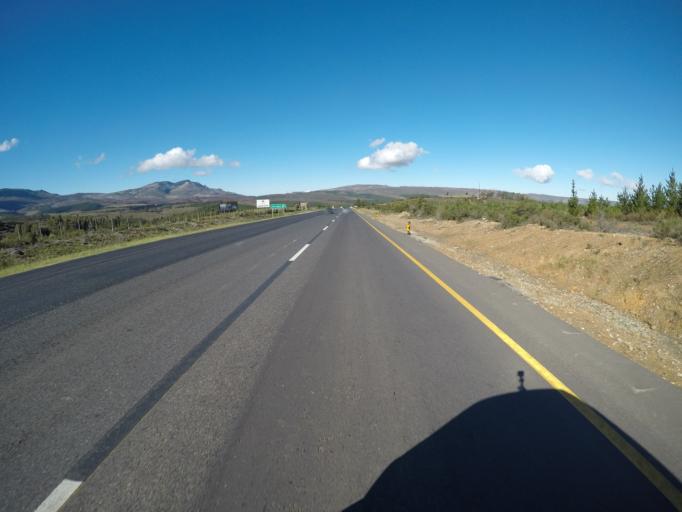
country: ZA
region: Western Cape
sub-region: Overberg District Municipality
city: Grabouw
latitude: -34.1812
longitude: 19.0815
